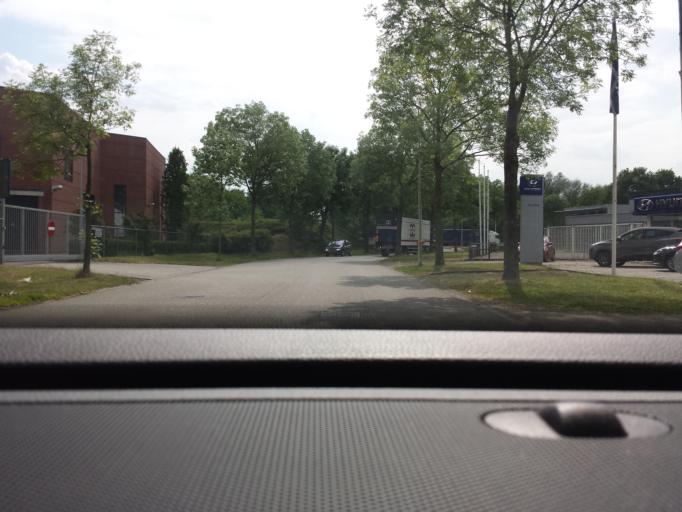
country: NL
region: Gelderland
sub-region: Gemeente Doetinchem
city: Doetinchem
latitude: 51.9694
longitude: 6.2613
